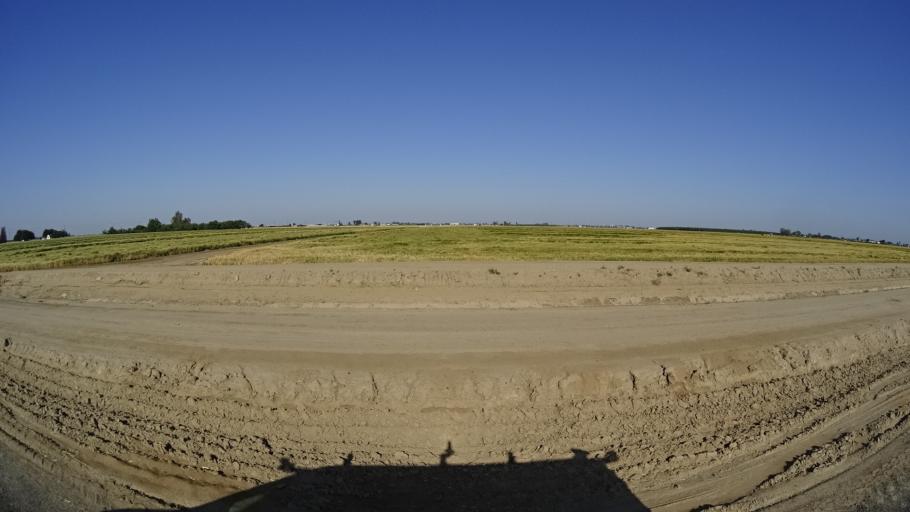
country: US
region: California
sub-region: Kings County
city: Home Garden
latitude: 36.3026
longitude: -119.5652
